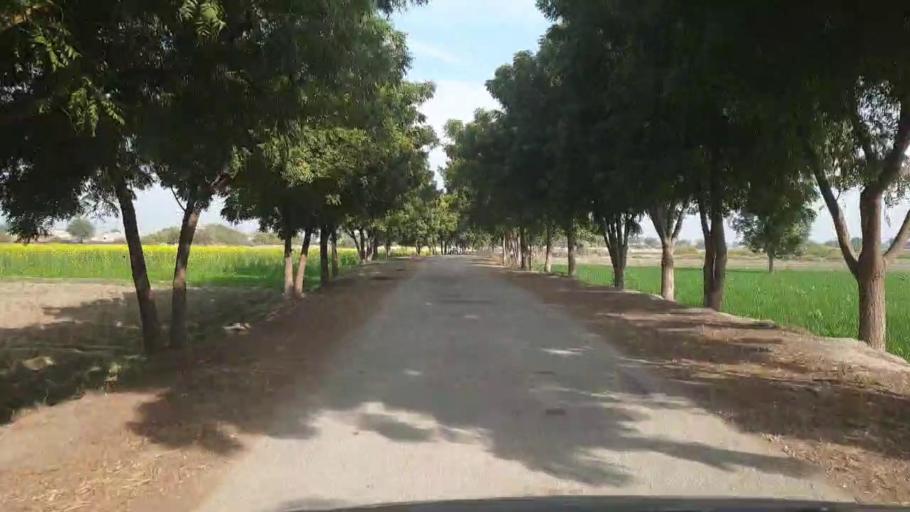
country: PK
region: Sindh
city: Khadro
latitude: 26.1551
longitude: 68.6951
